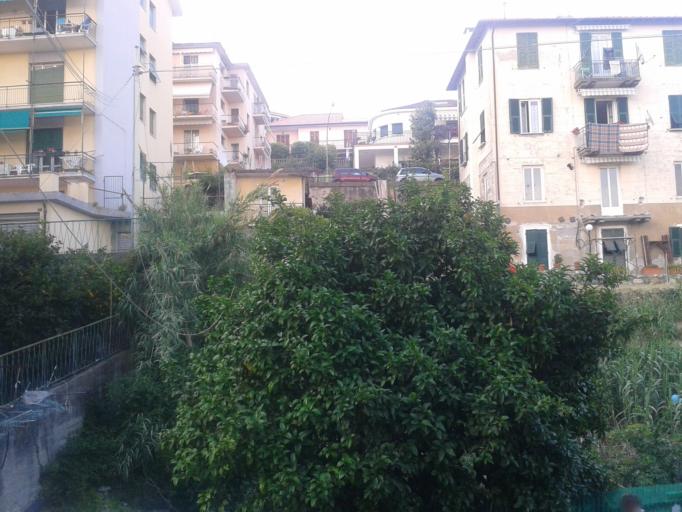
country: IT
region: Liguria
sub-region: Provincia di Savona
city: Varazze
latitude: 44.3614
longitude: 8.5854
